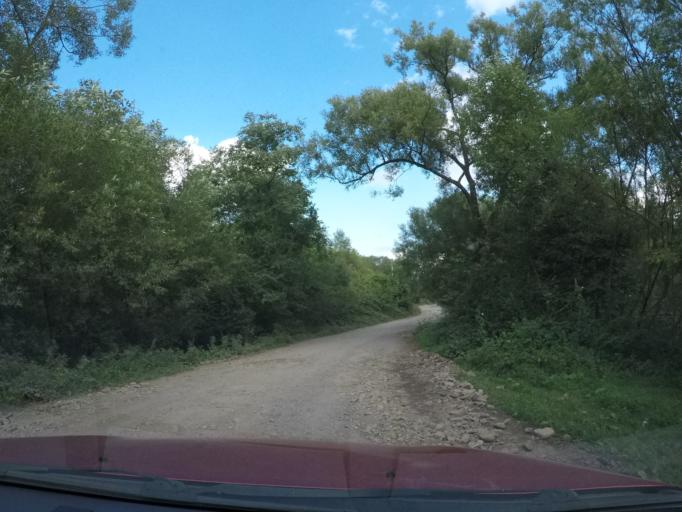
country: UA
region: Zakarpattia
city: Velykyi Bereznyi
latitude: 49.0257
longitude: 22.6054
